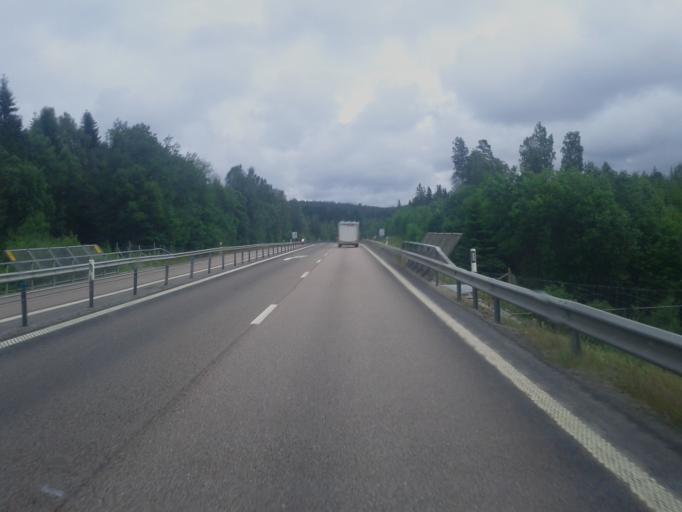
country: SE
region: Vaesternorrland
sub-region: Timra Kommun
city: Soraker
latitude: 62.5603
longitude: 17.7010
